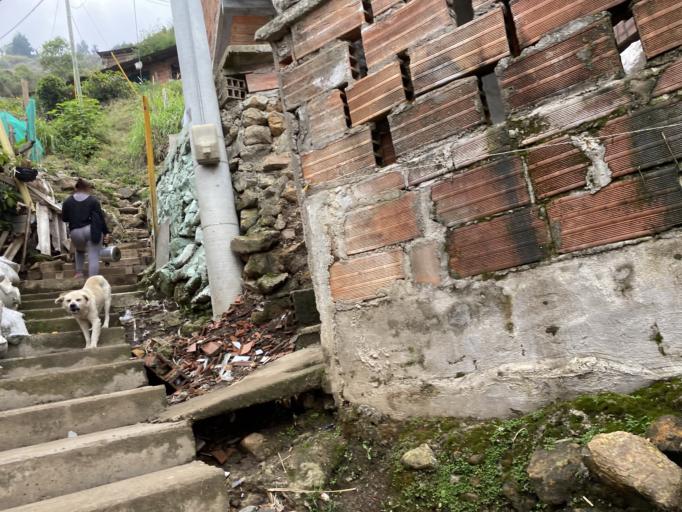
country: CO
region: Antioquia
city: Medellin
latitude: 6.2625
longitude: -75.5400
